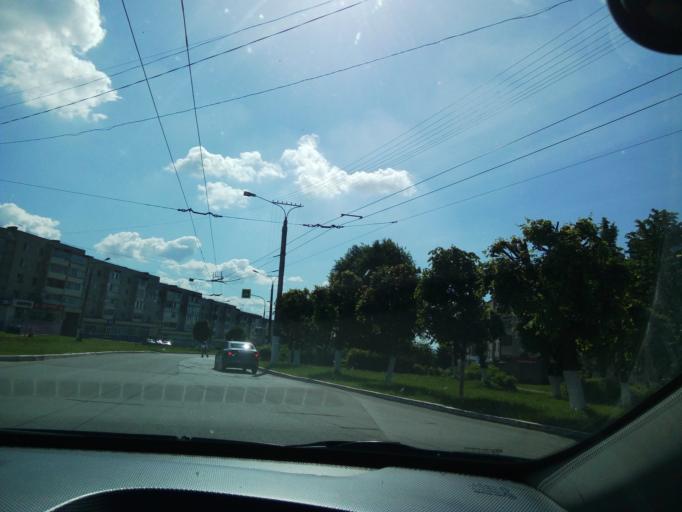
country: RU
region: Chuvashia
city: Novocheboksarsk
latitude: 56.1137
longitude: 47.4869
